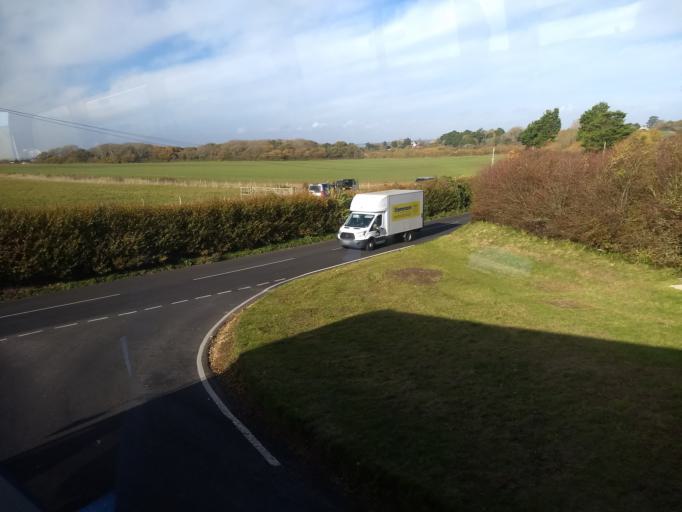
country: GB
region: England
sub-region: Isle of Wight
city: Yarmouth
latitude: 50.6981
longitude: -1.4818
